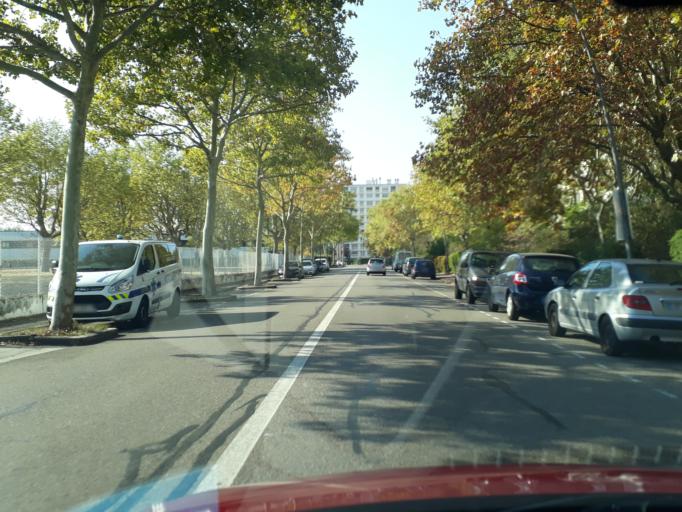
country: FR
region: Rhone-Alpes
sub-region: Departement du Rhone
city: Saint-Priest
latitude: 45.6863
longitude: 4.9409
